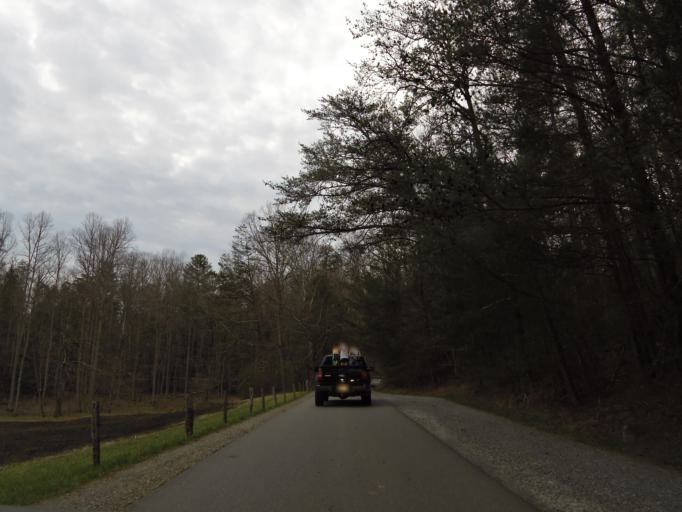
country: US
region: Tennessee
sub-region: Blount County
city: Wildwood
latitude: 35.6058
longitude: -83.8037
